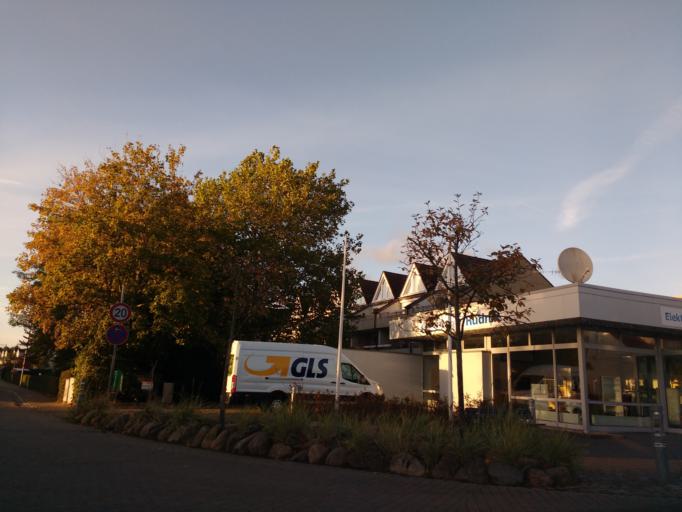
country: DE
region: Schleswig-Holstein
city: Kellenhusen
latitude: 54.1904
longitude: 11.0599
